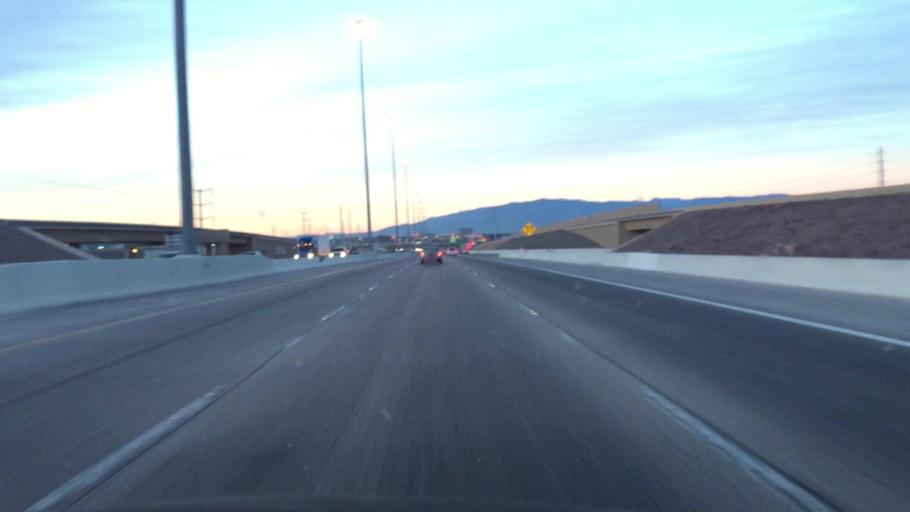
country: US
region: Nevada
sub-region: Clark County
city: Whitney
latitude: 36.0647
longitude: -115.0323
